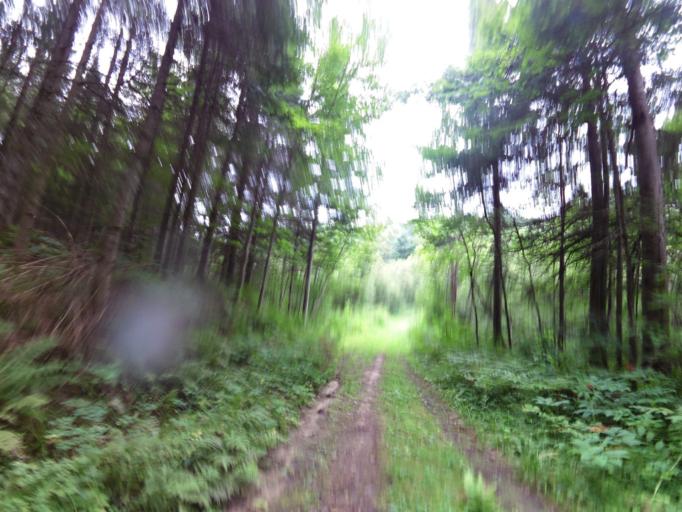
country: CA
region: Quebec
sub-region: Outaouais
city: Wakefield
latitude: 45.6170
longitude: -76.0374
